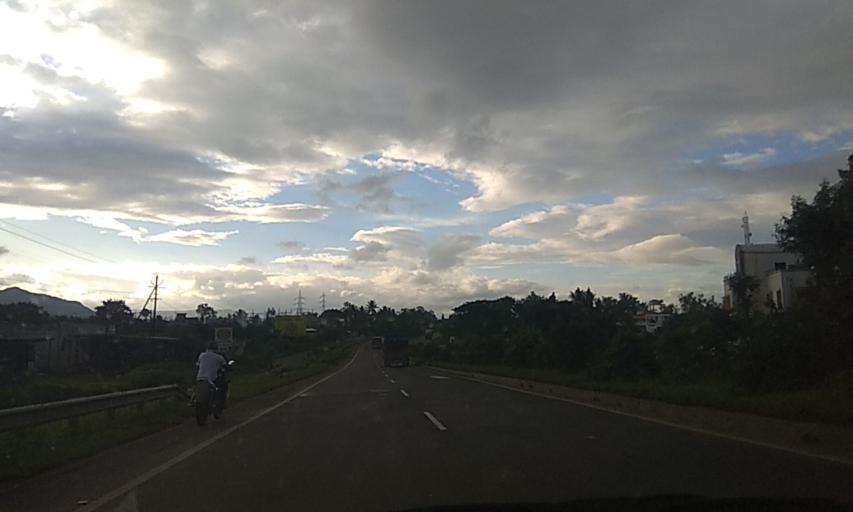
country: IN
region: Maharashtra
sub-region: Satara Division
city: Rahimatpur
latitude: 17.5271
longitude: 74.0679
